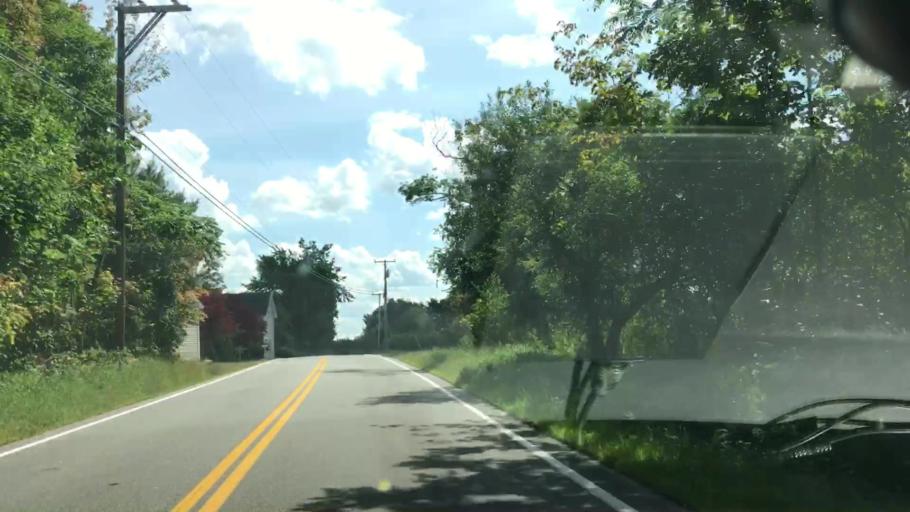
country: US
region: New Hampshire
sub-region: Hillsborough County
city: Bedford
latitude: 42.9236
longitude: -71.5735
